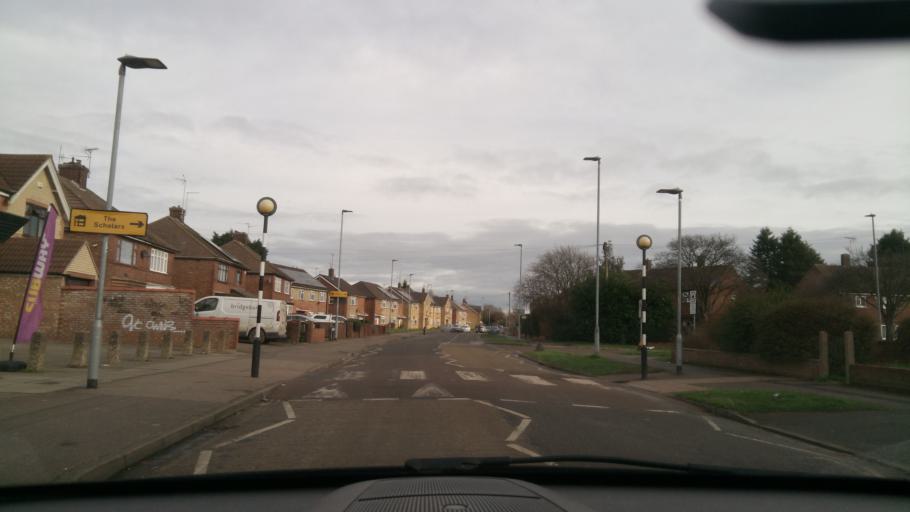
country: GB
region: England
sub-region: Peterborough
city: Peterborough
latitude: 52.6011
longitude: -0.2327
